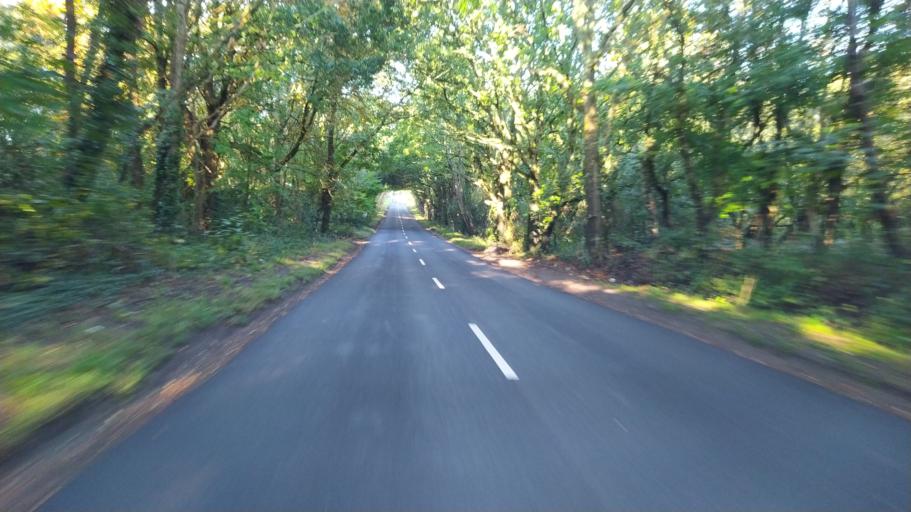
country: GB
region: England
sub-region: Dorset
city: Three Legged Cross
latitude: 50.8537
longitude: -1.9000
